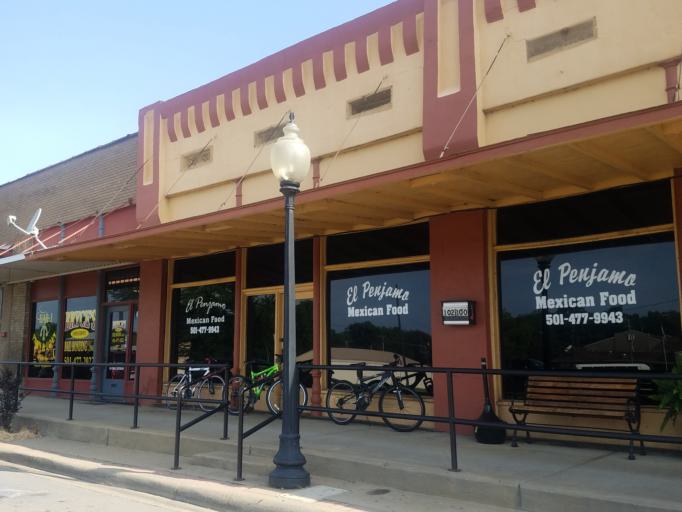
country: US
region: Arkansas
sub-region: Conway County
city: Morrilton
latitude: 35.1524
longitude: -92.7453
